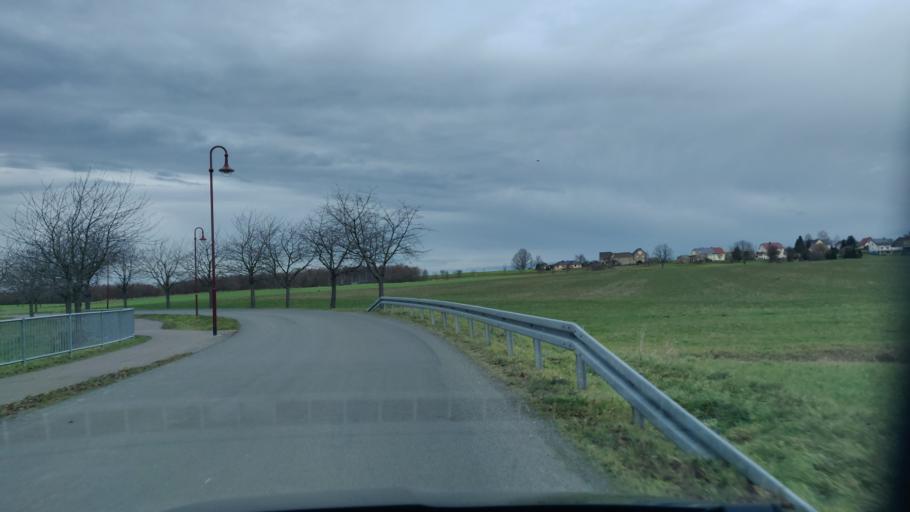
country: DE
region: Saxony
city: Bad Lausick
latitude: 51.1554
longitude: 12.6560
